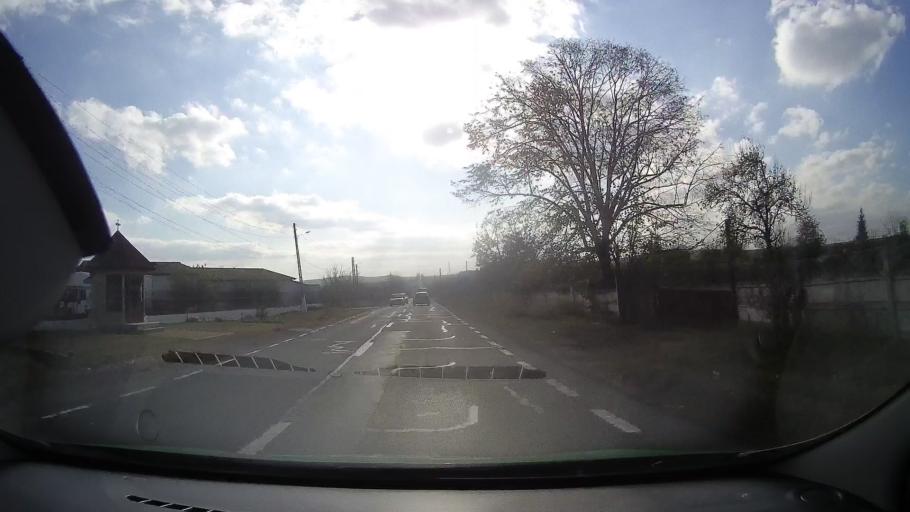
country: RO
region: Tulcea
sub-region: Comuna Nalbant
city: Nalbant
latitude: 45.0522
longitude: 28.6175
